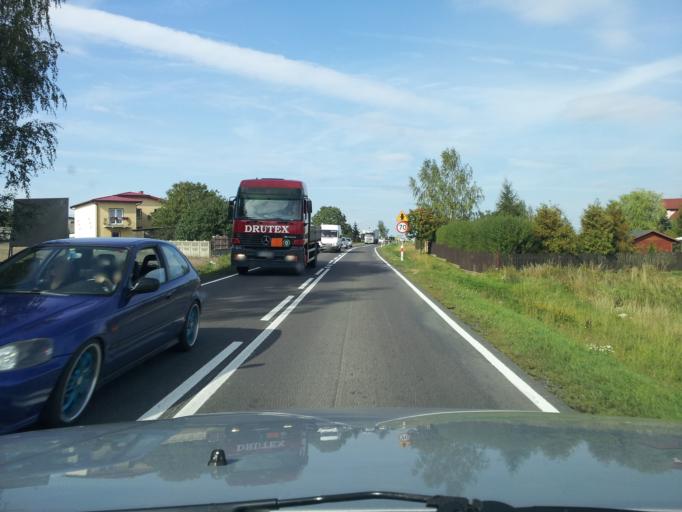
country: PL
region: Warmian-Masurian Voivodeship
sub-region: Powiat ilawski
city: Lubawa
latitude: 53.5324
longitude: 19.7489
